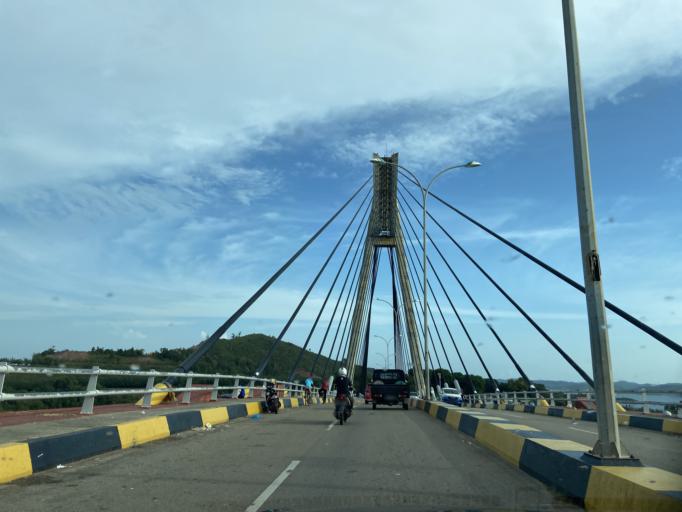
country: SG
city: Singapore
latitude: 0.9813
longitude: 104.0414
